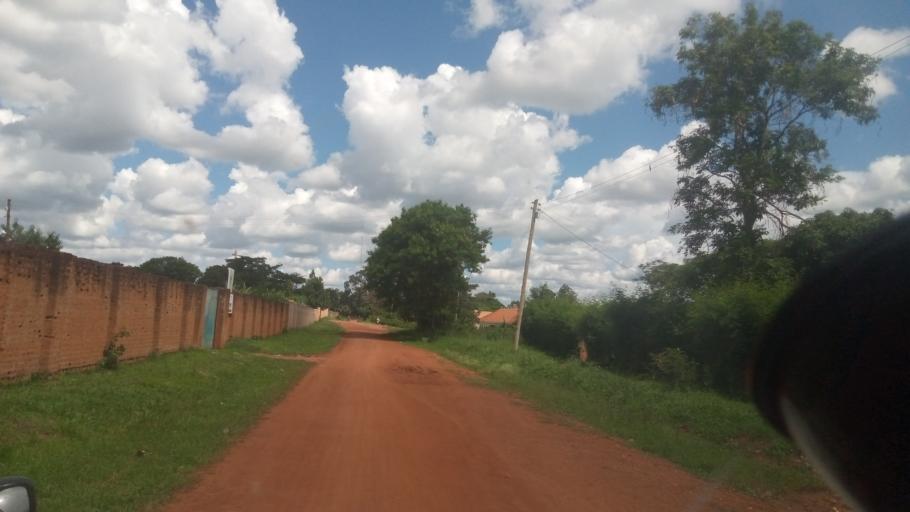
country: UG
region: Northern Region
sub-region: Lira District
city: Lira
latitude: 2.2415
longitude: 32.9017
